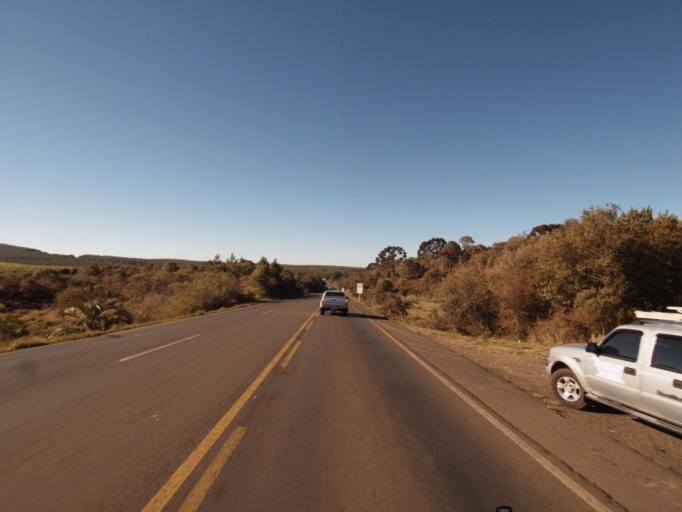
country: BR
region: Santa Catarina
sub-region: Concordia
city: Concordia
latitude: -26.9169
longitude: -51.9573
